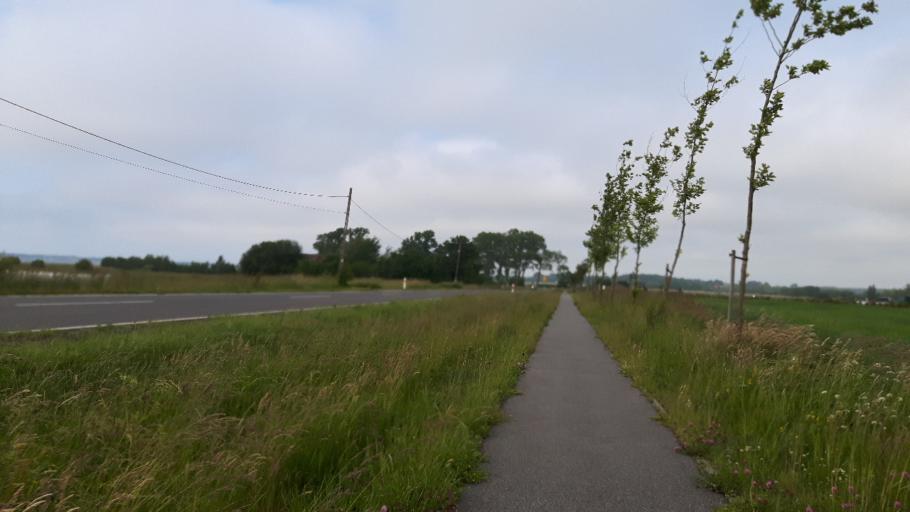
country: PL
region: West Pomeranian Voivodeship
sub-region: Powiat koszalinski
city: Sianow
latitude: 54.3390
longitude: 16.3191
